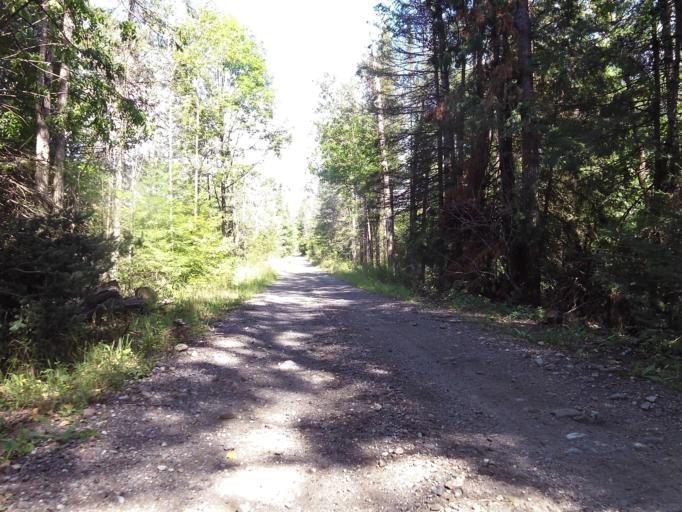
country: CA
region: Ontario
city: Renfrew
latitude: 45.0846
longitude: -76.7209
